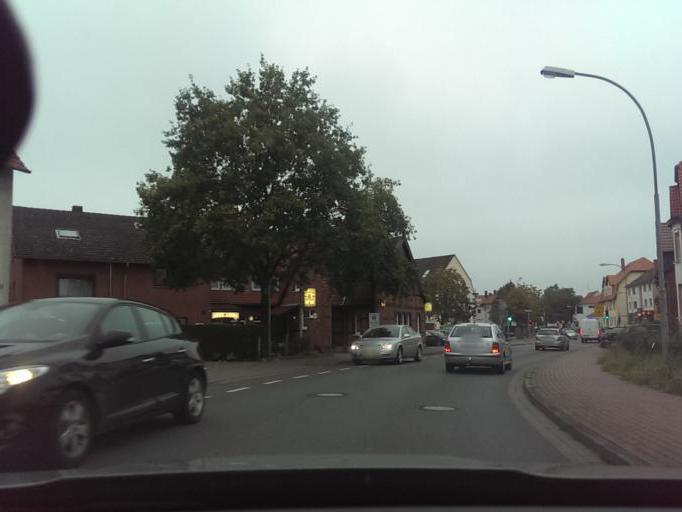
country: DE
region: Lower Saxony
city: Garbsen
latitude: 52.4130
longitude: 9.5883
